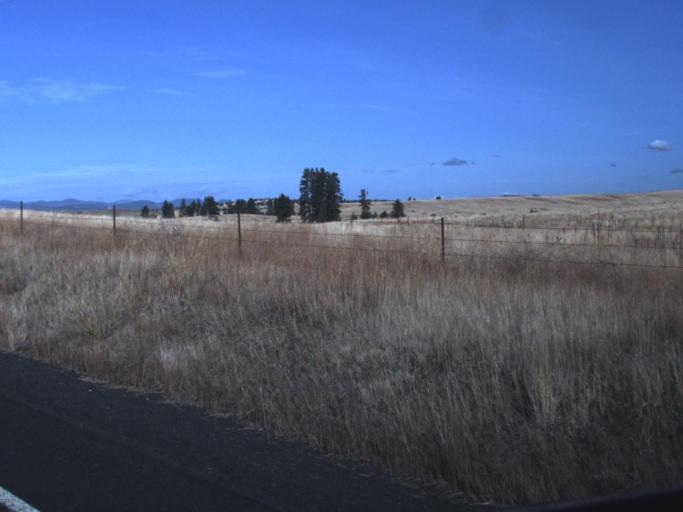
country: US
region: Washington
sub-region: Lincoln County
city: Davenport
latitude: 47.7505
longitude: -118.1727
